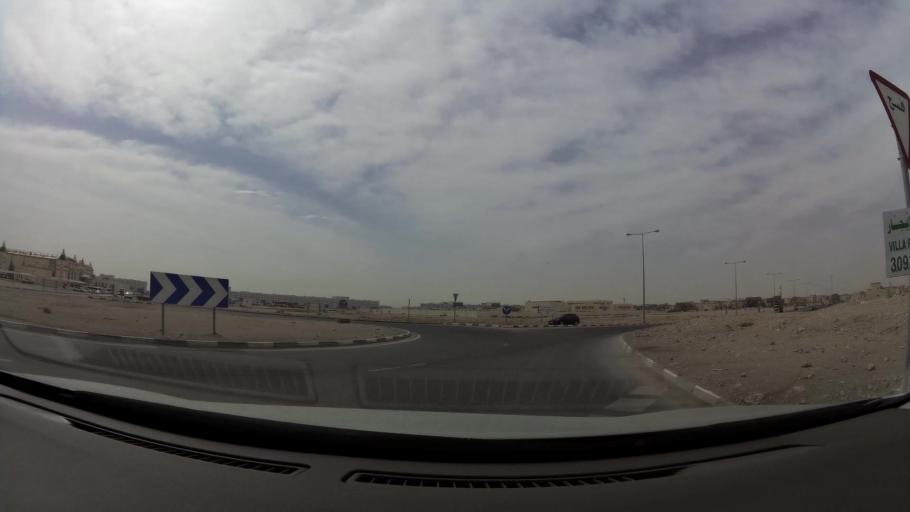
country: QA
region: Baladiyat ad Dawhah
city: Doha
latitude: 25.2202
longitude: 51.4936
